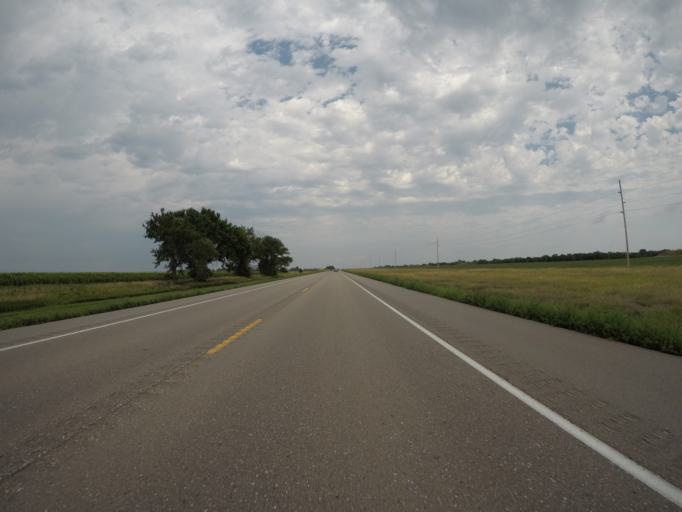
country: US
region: Nebraska
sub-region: Clay County
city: Harvard
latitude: 40.5827
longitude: -98.1775
